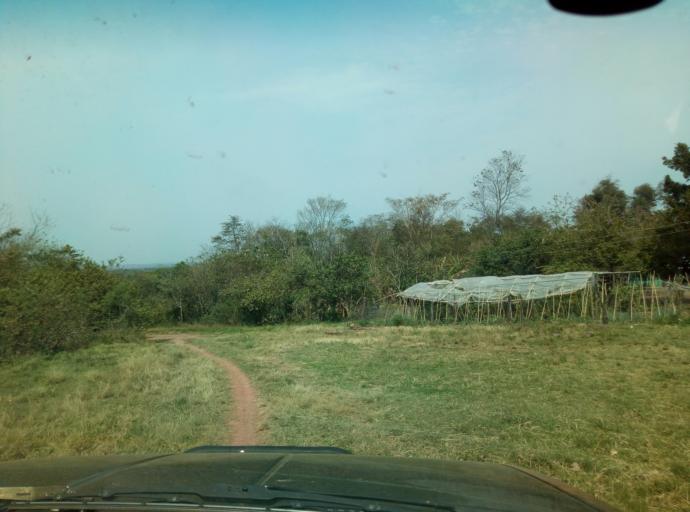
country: PY
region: Caaguazu
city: Yhu
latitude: -25.1765
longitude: -56.0902
